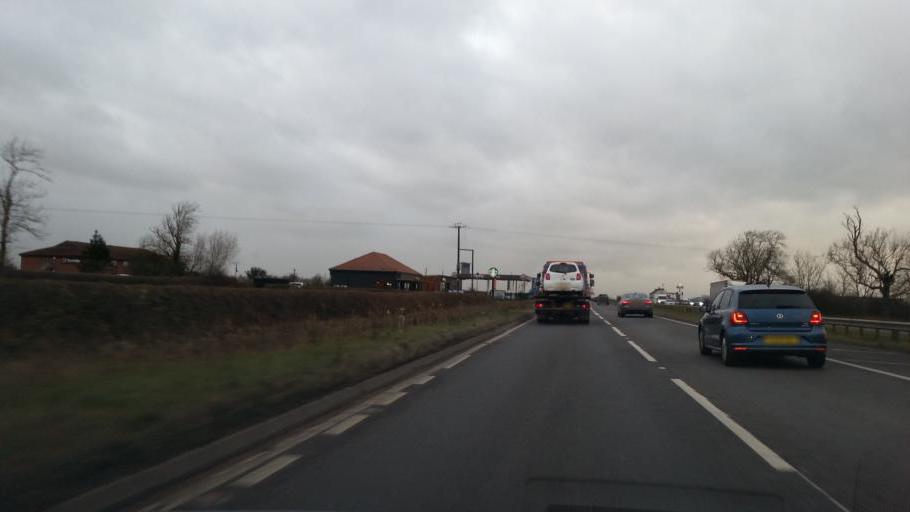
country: GB
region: England
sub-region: District of Rutland
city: Greetham
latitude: 52.7625
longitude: -0.6107
